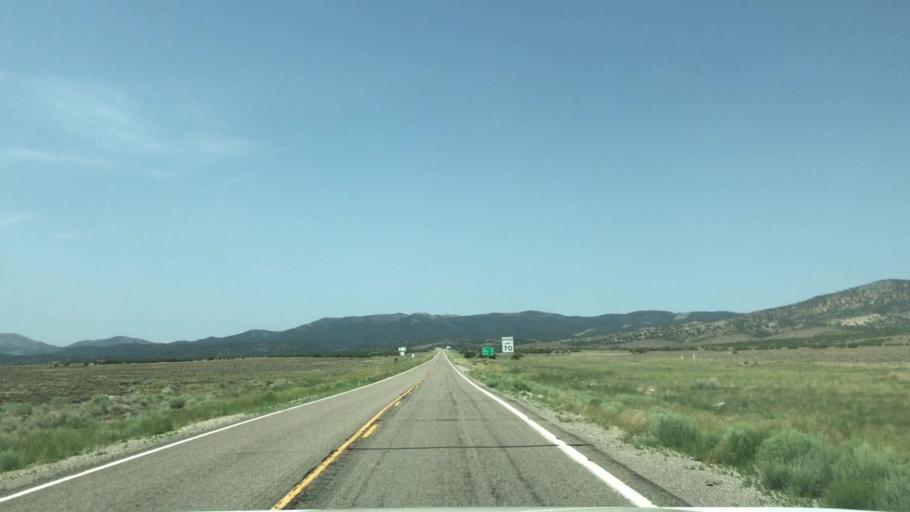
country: US
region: Nevada
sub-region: White Pine County
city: Ely
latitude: 39.0358
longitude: -114.5502
